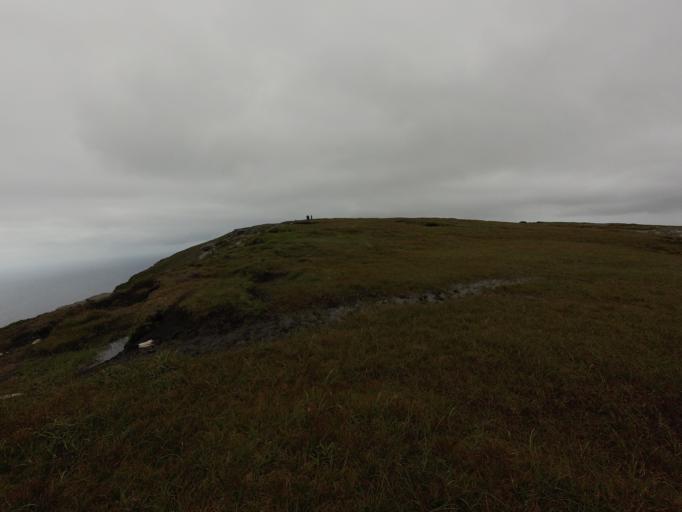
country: IE
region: Ulster
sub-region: County Donegal
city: Killybegs
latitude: 54.6483
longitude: -8.6921
